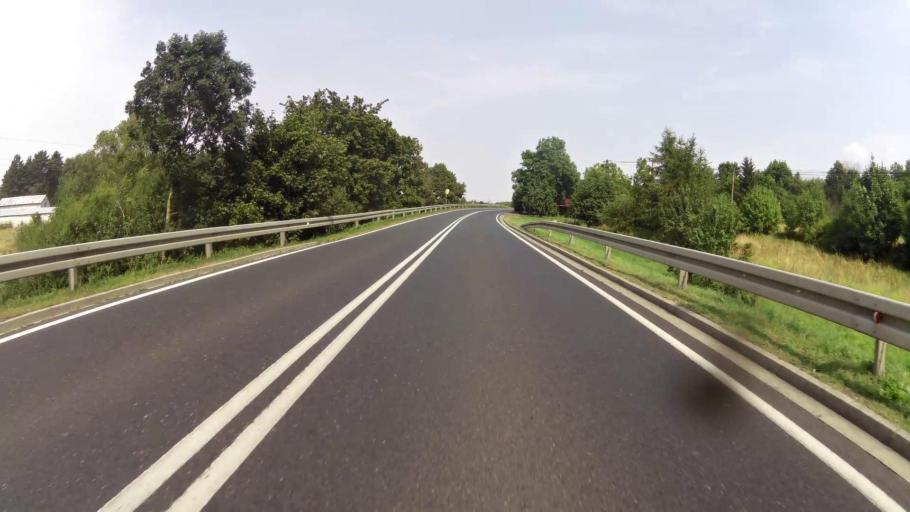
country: PL
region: West Pomeranian Voivodeship
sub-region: Powiat mysliborski
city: Mysliborz
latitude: 52.9325
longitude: 14.8924
